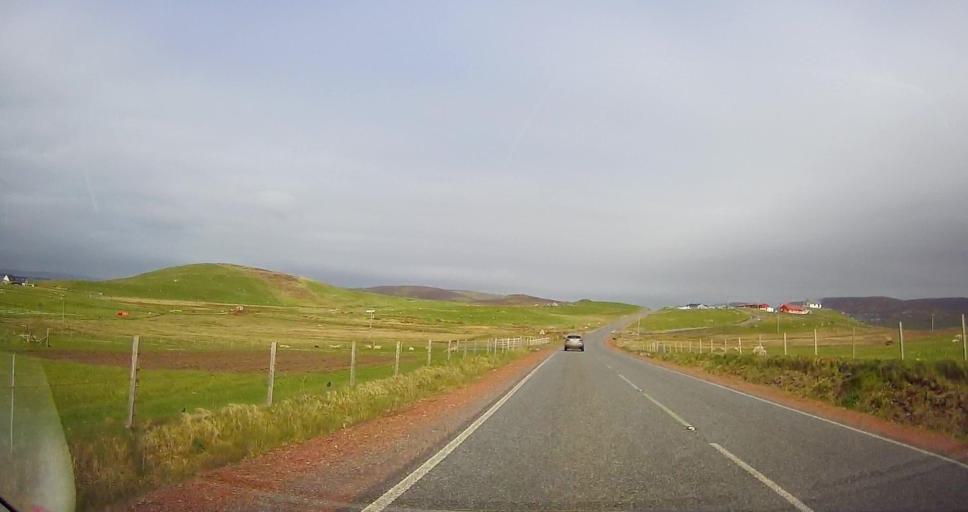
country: GB
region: Scotland
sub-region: Shetland Islands
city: Sandwick
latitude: 60.1147
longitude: -1.2939
